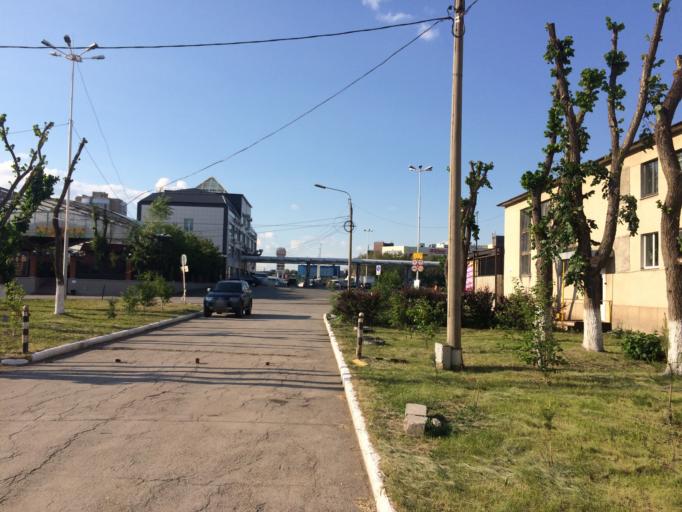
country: RU
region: Chelyabinsk
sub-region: Gorod Magnitogorsk
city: Magnitogorsk
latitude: 53.3996
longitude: 58.9865
